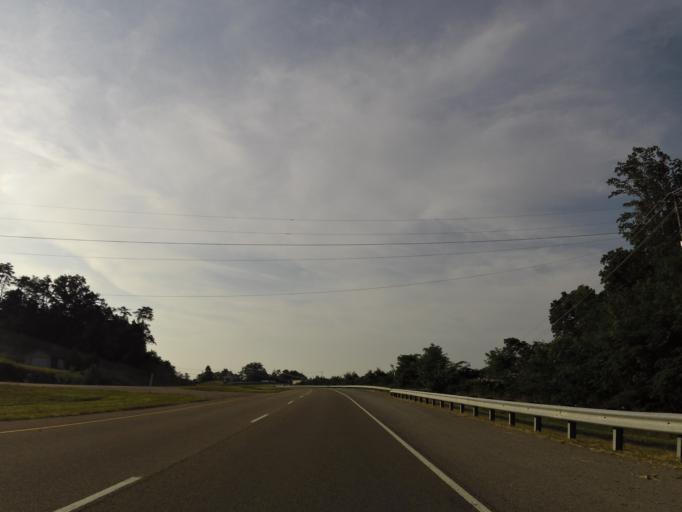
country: US
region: Tennessee
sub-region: Loudon County
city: Lenoir City
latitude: 35.7530
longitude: -84.2160
